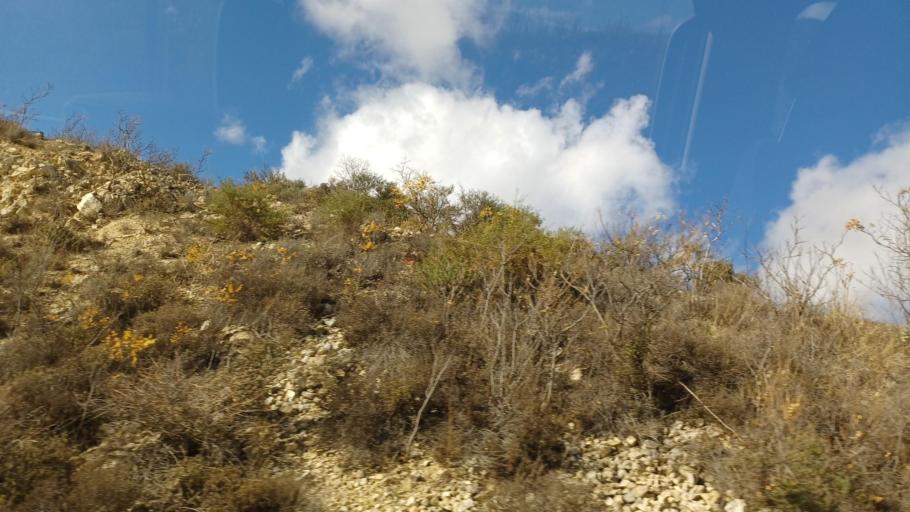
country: CY
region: Limassol
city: Pachna
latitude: 34.8490
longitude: 32.8050
